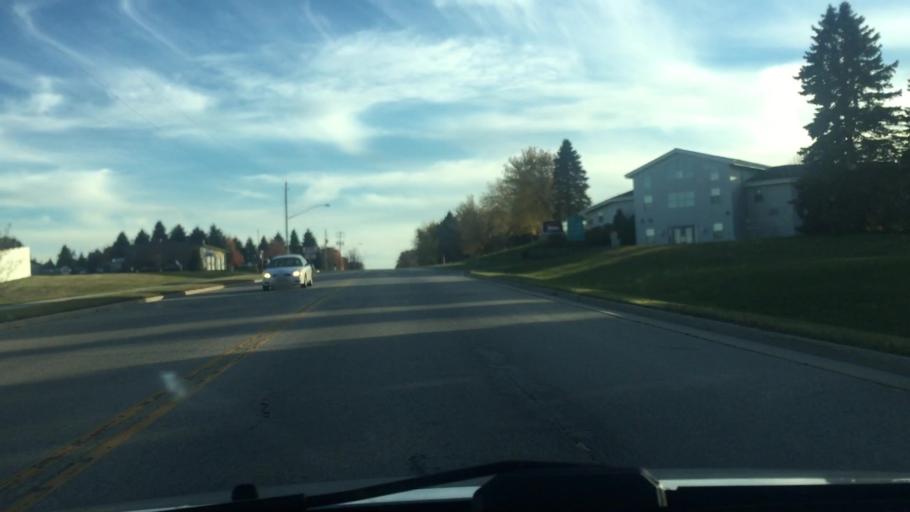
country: US
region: Wisconsin
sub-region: Manitowoc County
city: Mishicot
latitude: 44.2381
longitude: -87.6454
